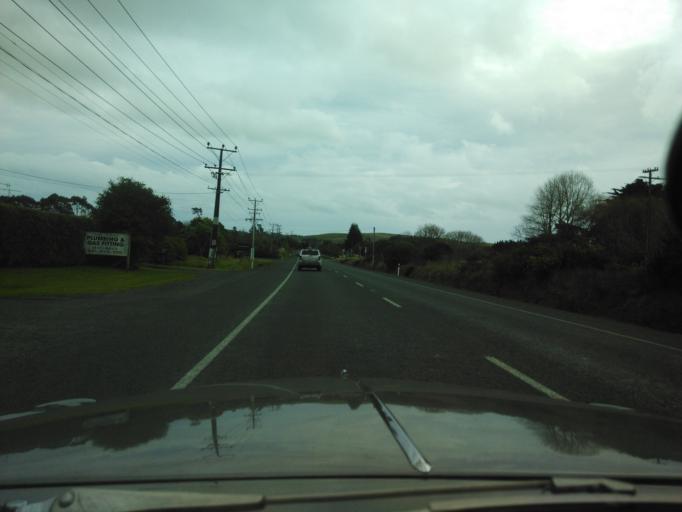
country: NZ
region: Auckland
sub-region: Auckland
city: Muriwai Beach
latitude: -36.7663
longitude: 174.5053
